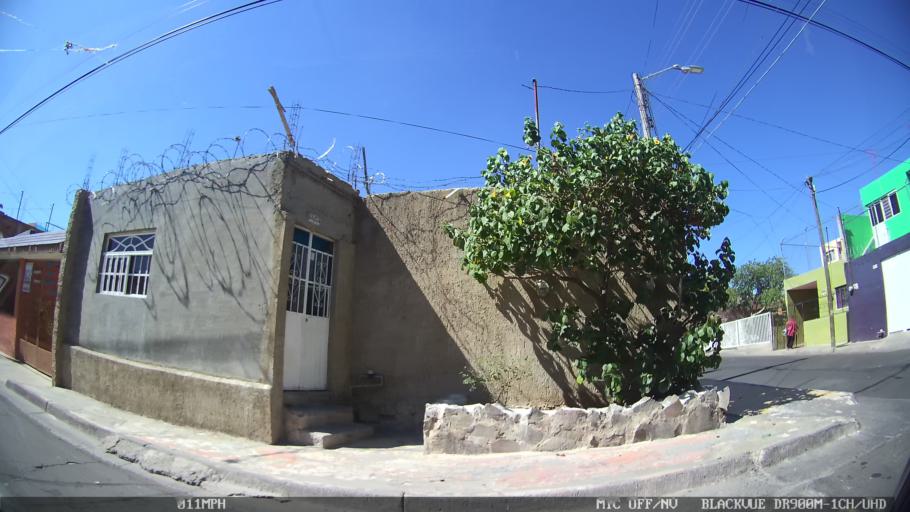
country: MX
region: Jalisco
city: Tlaquepaque
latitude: 20.6979
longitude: -103.2791
